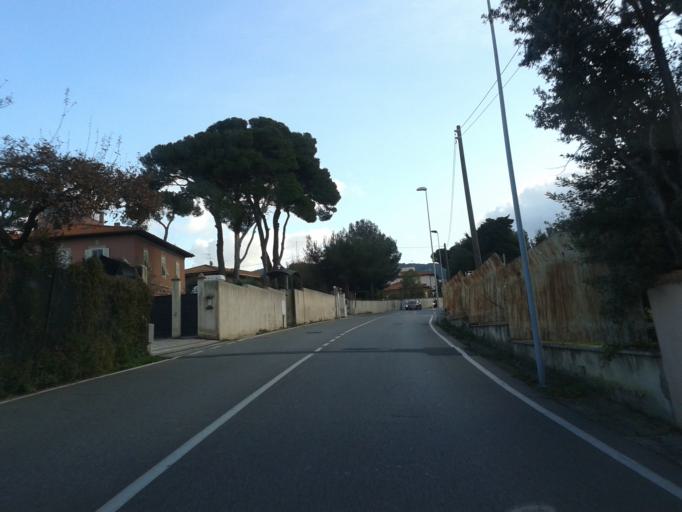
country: IT
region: Tuscany
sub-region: Provincia di Livorno
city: Livorno
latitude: 43.5085
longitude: 10.3357
